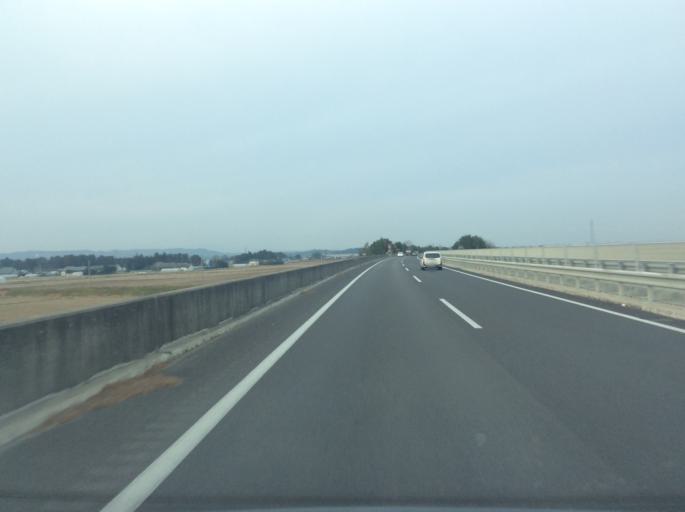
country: JP
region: Miyagi
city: Iwanuma
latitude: 38.1175
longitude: 140.8872
